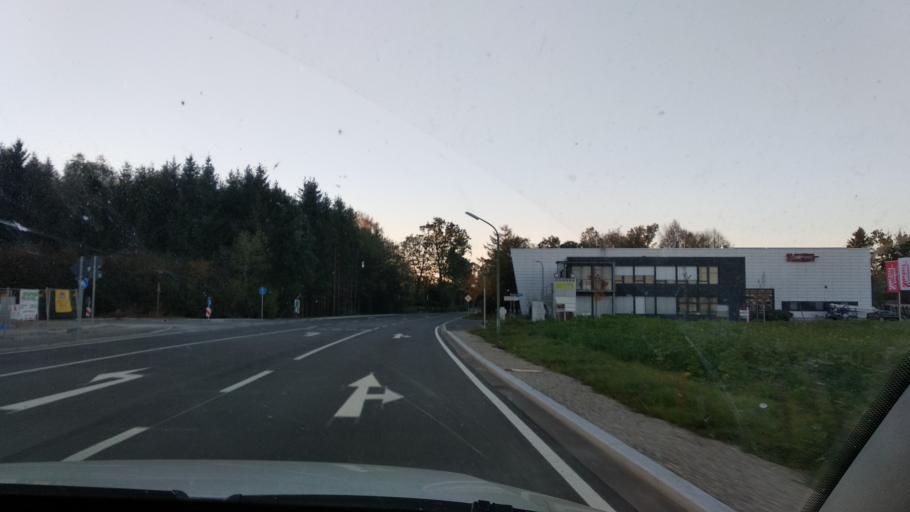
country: DE
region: Bavaria
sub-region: Upper Bavaria
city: Hohenkirchen-Siegertsbrunn
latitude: 48.0335
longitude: 11.7168
